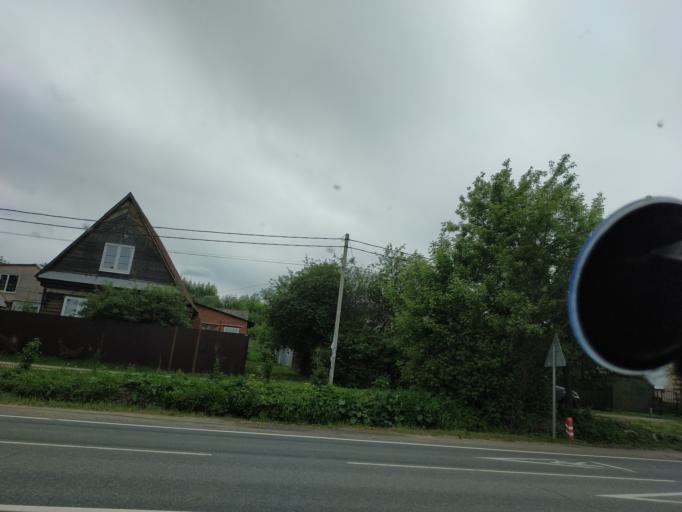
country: RU
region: Moskovskaya
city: Ostrovtsy
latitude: 55.5558
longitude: 38.0571
